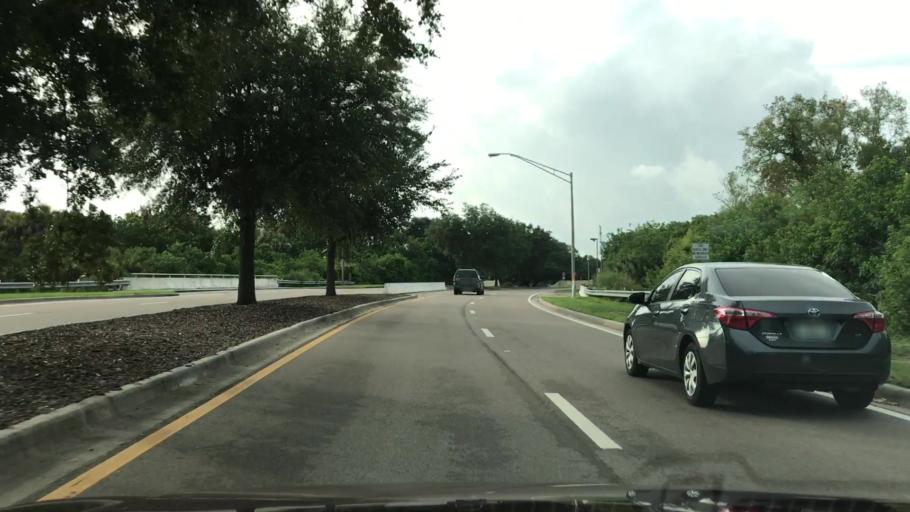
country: US
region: Florida
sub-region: Sarasota County
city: Venice Gardens
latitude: 27.0578
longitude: -82.3950
